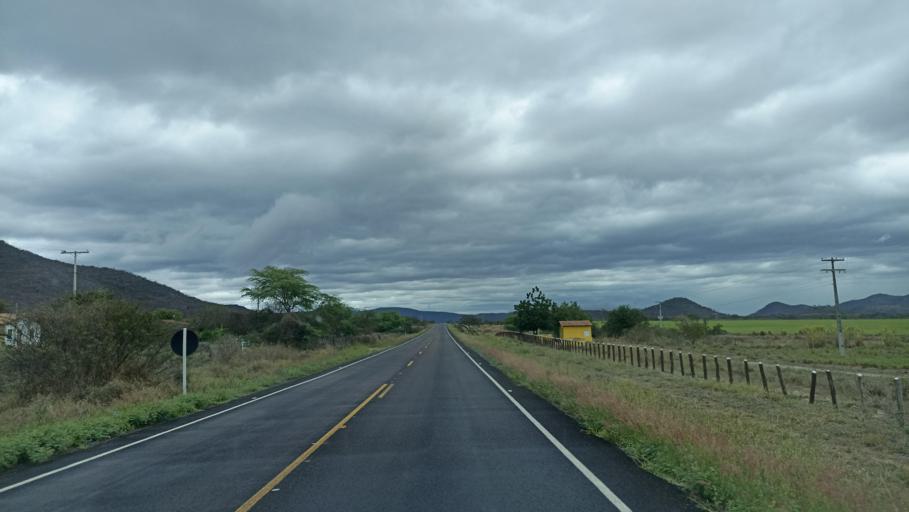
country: BR
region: Bahia
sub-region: Iacu
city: Iacu
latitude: -12.8928
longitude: -40.3976
